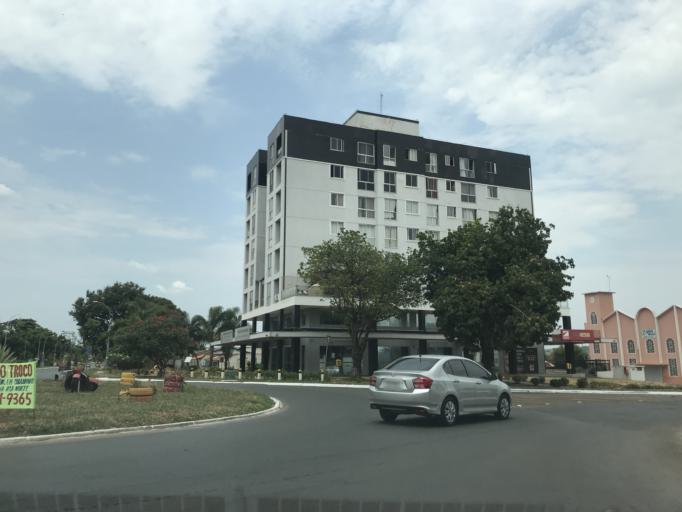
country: BR
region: Federal District
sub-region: Brasilia
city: Brasilia
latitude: -15.6473
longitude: -47.8033
